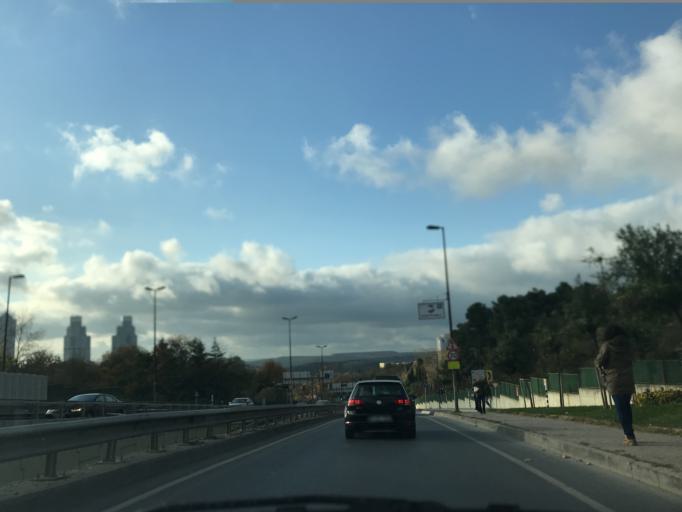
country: TR
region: Istanbul
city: Sisli
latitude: 41.1078
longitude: 29.0137
